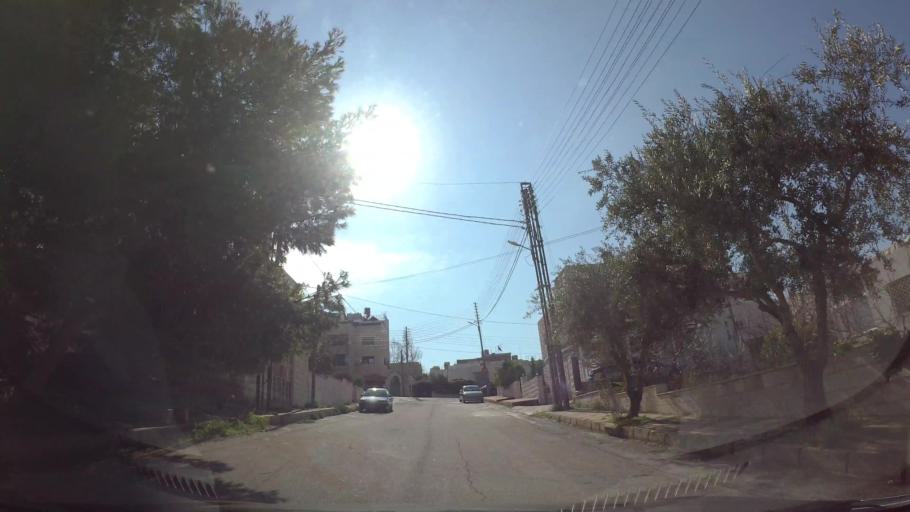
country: JO
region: Amman
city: Al Jubayhah
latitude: 32.0021
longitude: 35.8847
